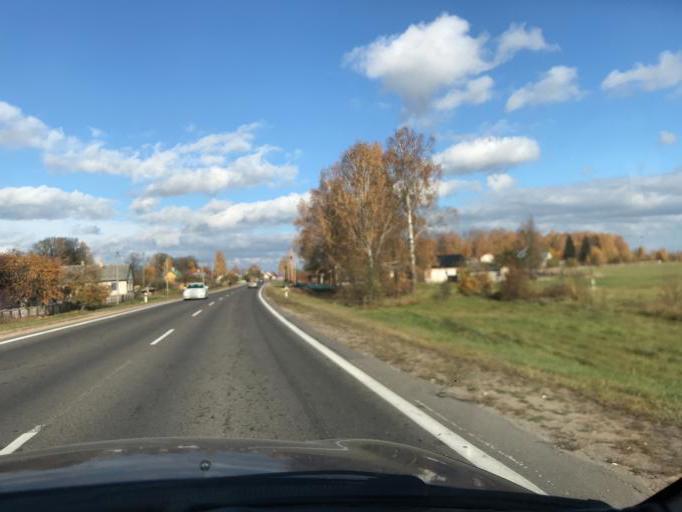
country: LT
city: Salcininkai
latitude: 54.2377
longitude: 25.3553
